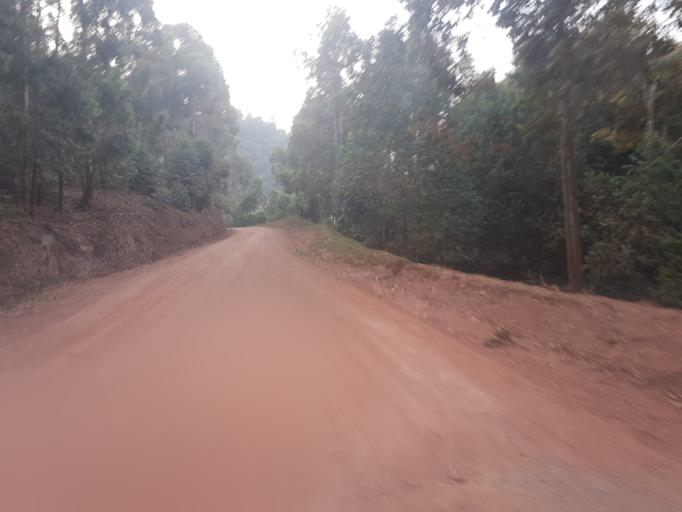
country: UG
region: Western Region
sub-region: Kanungu District
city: Kanungu
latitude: -0.9951
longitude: 29.8502
